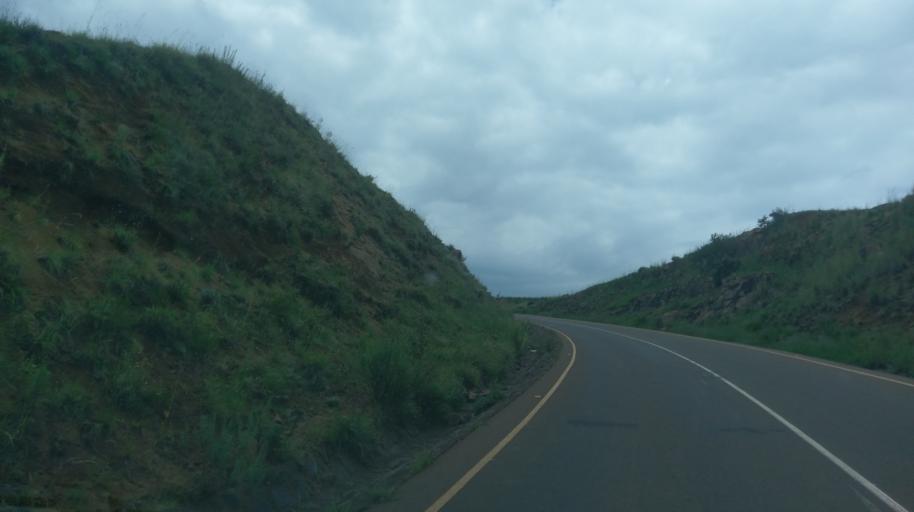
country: LS
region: Leribe
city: Leribe
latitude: -29.0370
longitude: 28.2514
